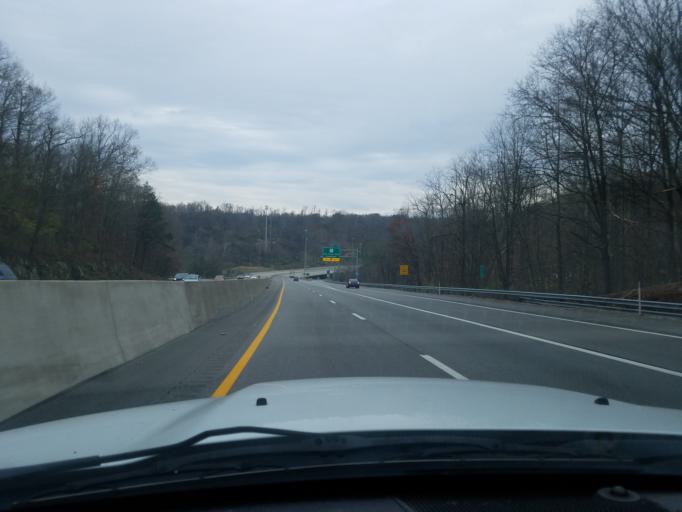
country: US
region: West Virginia
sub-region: Cabell County
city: Huntington
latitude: 38.3958
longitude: -82.4015
